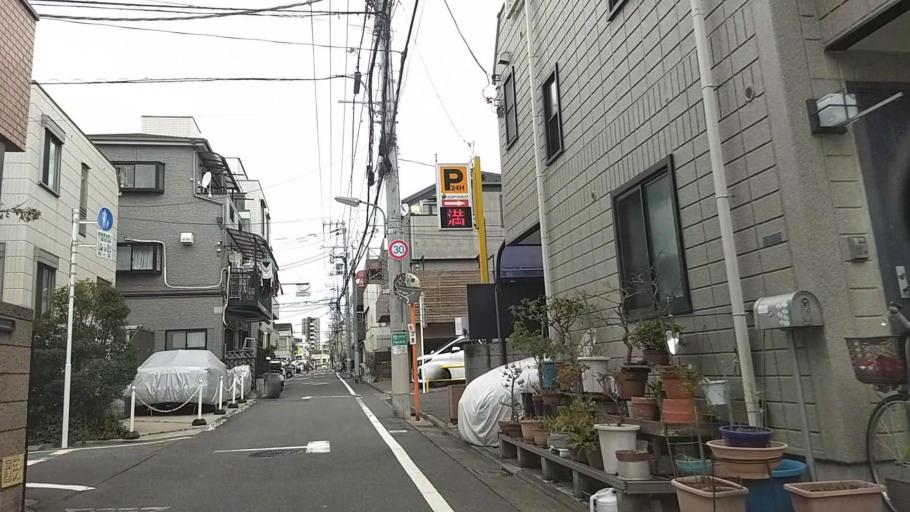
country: JP
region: Tokyo
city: Tokyo
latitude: 35.6100
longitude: 139.7239
